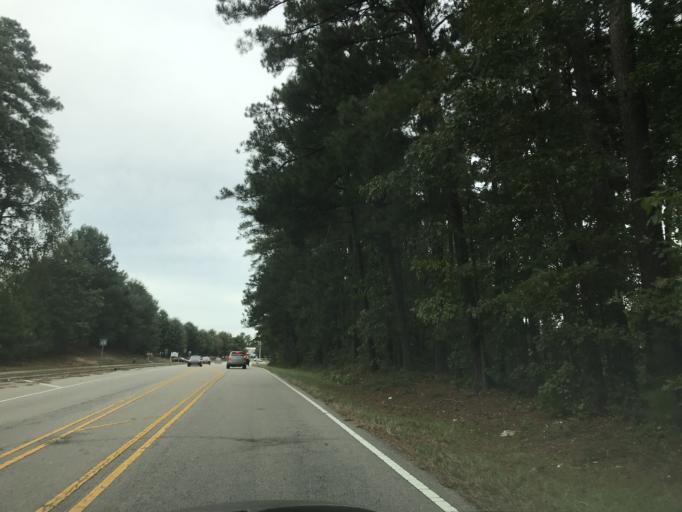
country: US
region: North Carolina
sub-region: Wake County
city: Rolesville
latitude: 35.8903
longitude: -78.5086
